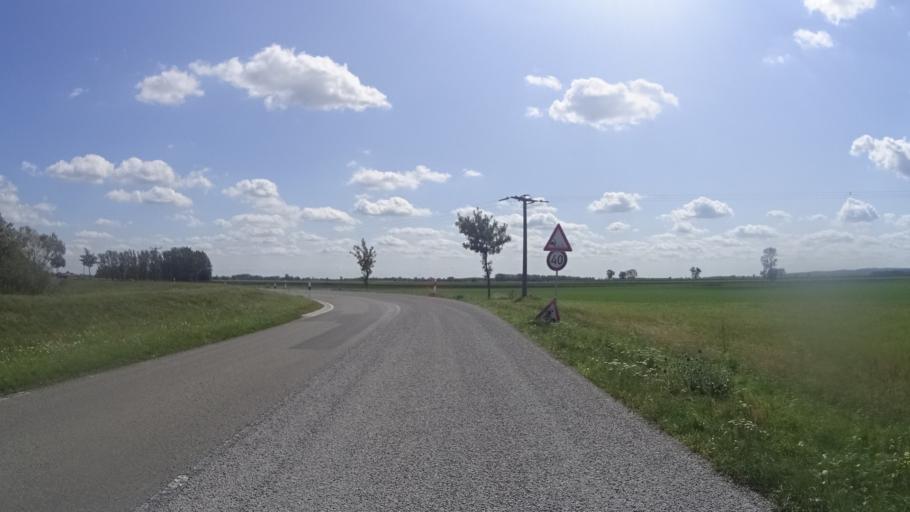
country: DE
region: Saxony-Anhalt
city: Kamern
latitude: 52.7909
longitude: 12.1697
